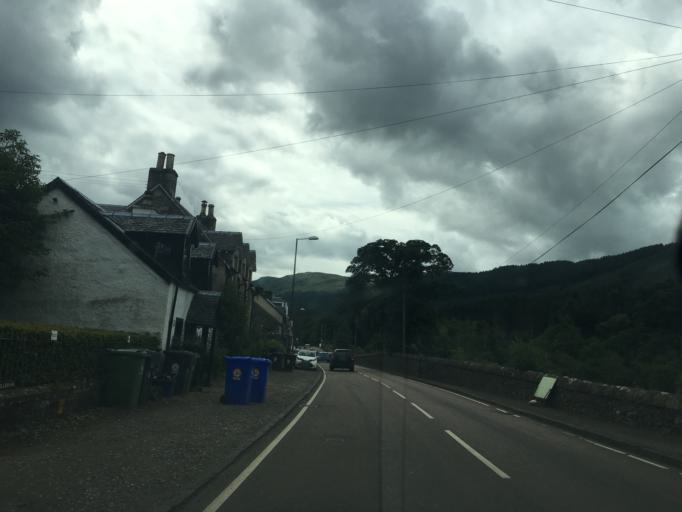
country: GB
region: Scotland
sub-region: Stirling
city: Callander
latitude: 56.3271
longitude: -4.3274
